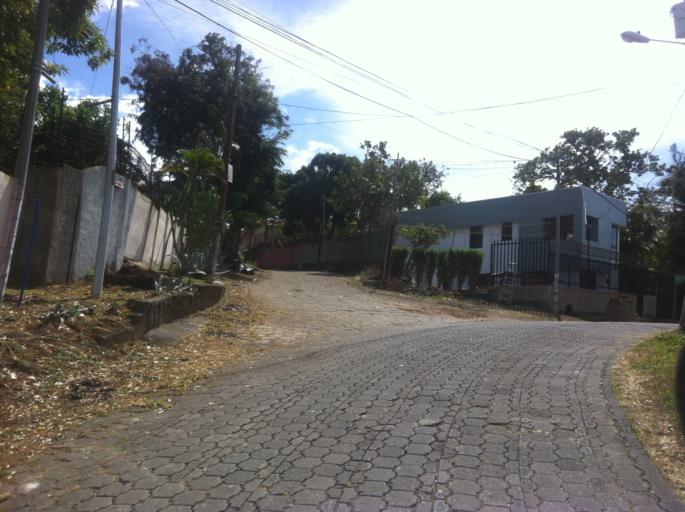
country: NI
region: Managua
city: El Crucero
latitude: 12.0724
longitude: -86.3231
